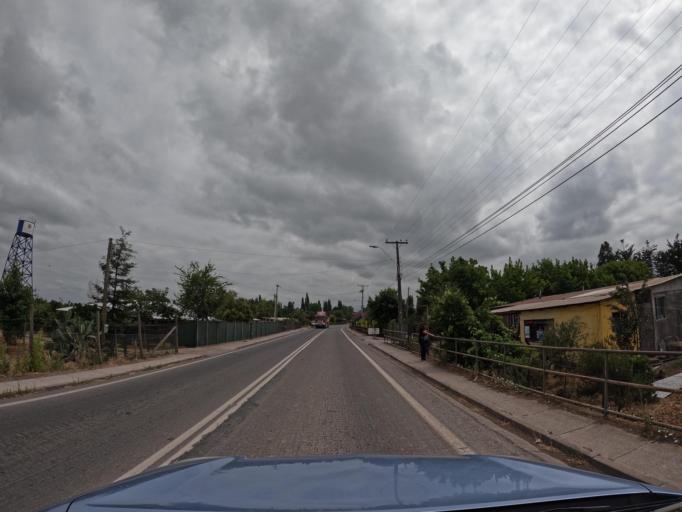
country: CL
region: Maule
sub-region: Provincia de Curico
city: Teno
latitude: -34.7517
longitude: -71.2386
